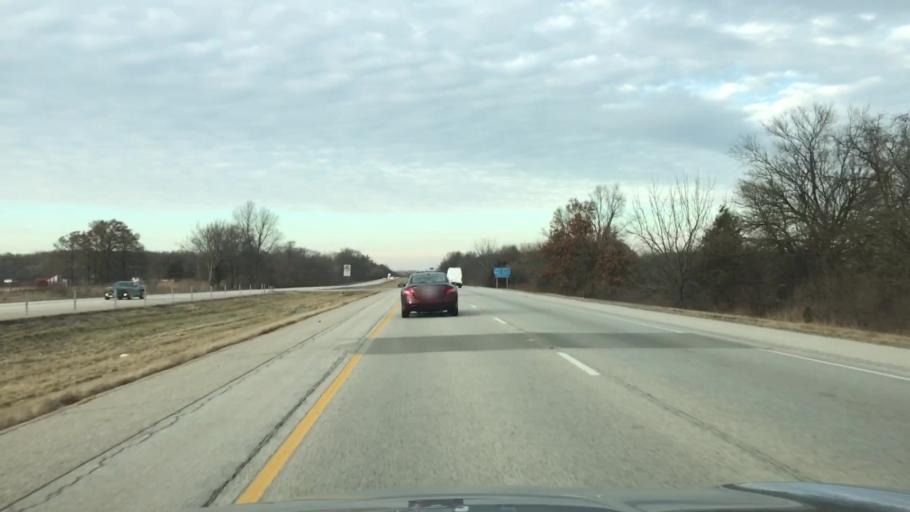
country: US
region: Illinois
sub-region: Sangamon County
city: Sherman
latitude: 39.8543
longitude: -89.5948
